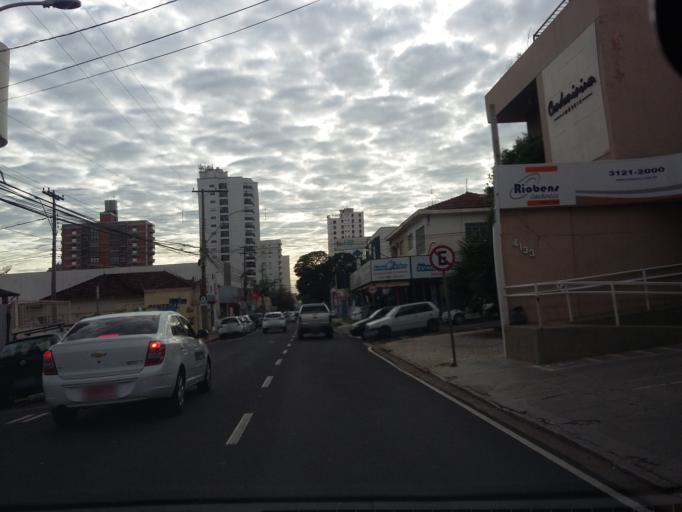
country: BR
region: Sao Paulo
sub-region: Sao Jose Do Rio Preto
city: Sao Jose do Rio Preto
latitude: -20.8187
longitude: -49.3885
